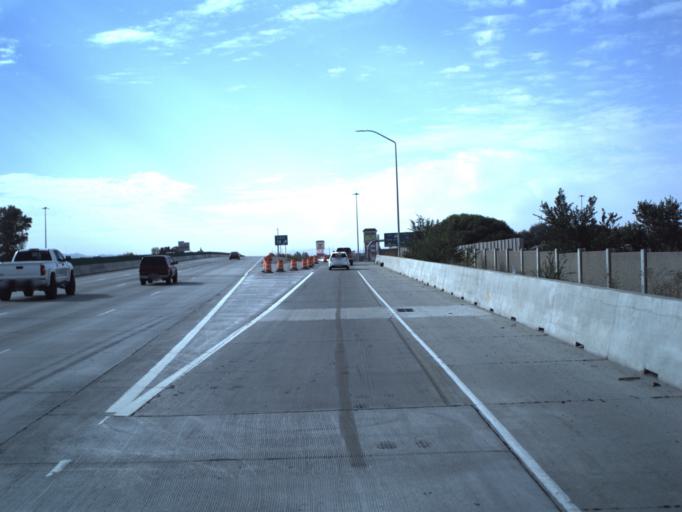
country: US
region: Utah
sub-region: Salt Lake County
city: Taylorsville
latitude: 40.7003
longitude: -111.9531
